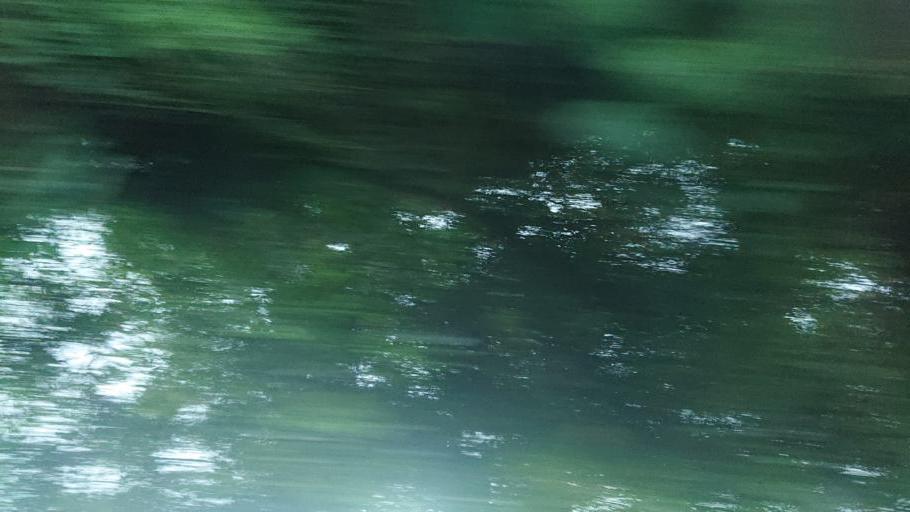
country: TW
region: Taiwan
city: Lugu
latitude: 23.5889
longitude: 120.7235
